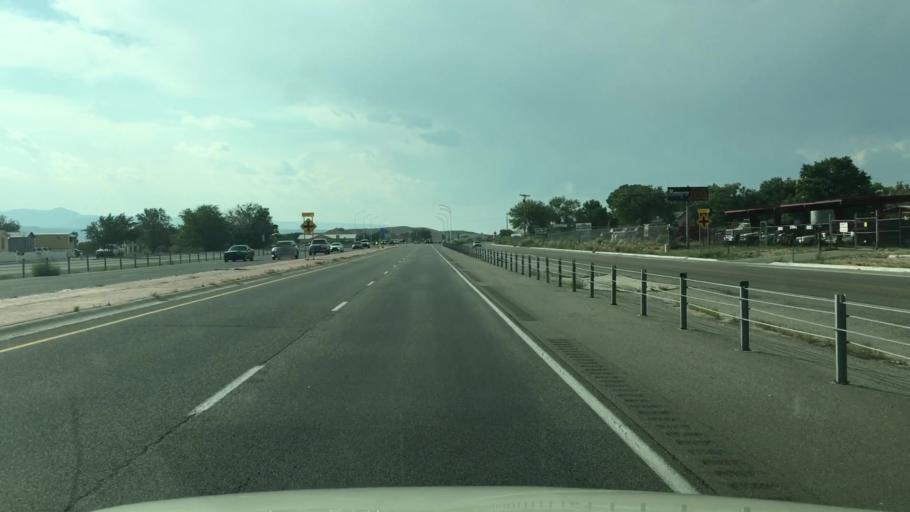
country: US
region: New Mexico
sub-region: Santa Fe County
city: El Valle de Arroyo Seco
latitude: 35.9667
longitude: -106.0345
